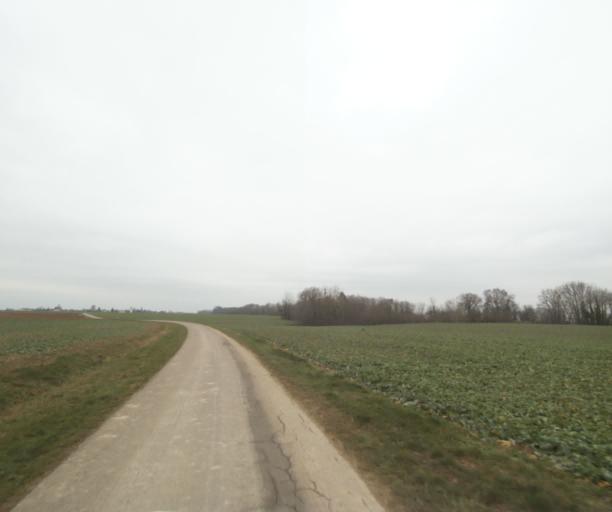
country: FR
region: Champagne-Ardenne
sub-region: Departement de la Haute-Marne
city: Villiers-en-Lieu
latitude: 48.6382
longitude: 4.7889
